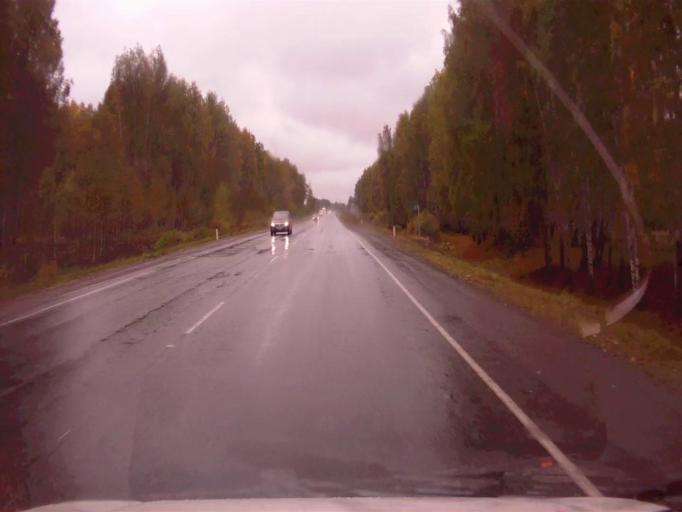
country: RU
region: Chelyabinsk
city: Argayash
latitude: 55.4654
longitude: 60.9118
